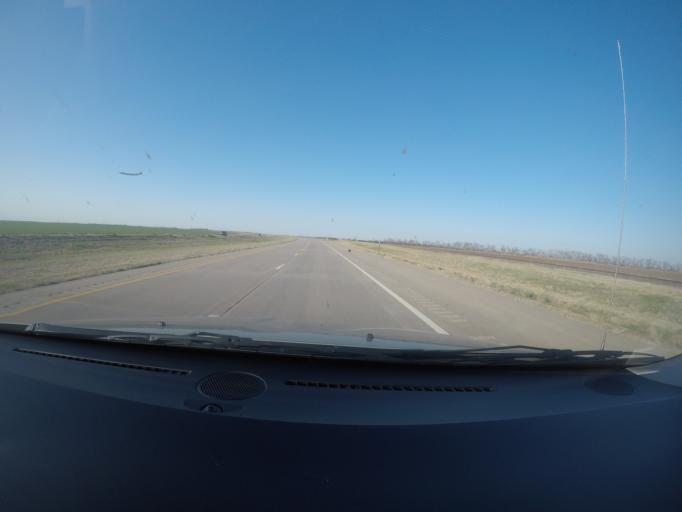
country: US
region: Kansas
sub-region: McPherson County
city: McPherson
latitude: 38.3065
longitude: -97.7171
